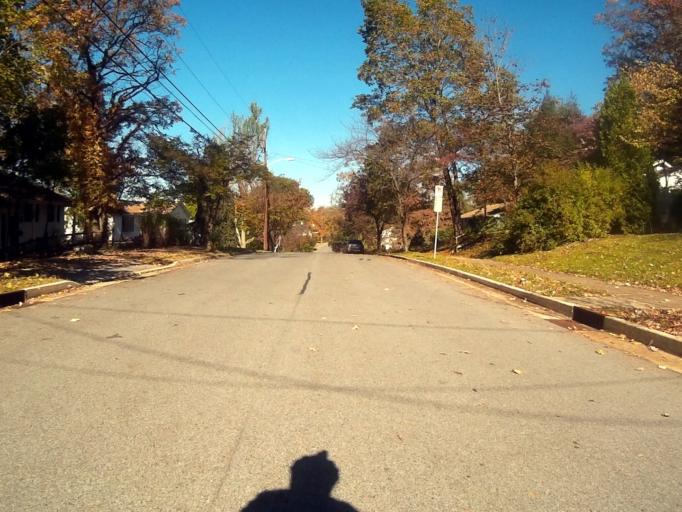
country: US
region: Pennsylvania
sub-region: Centre County
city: State College
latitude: 40.7983
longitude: -77.8814
